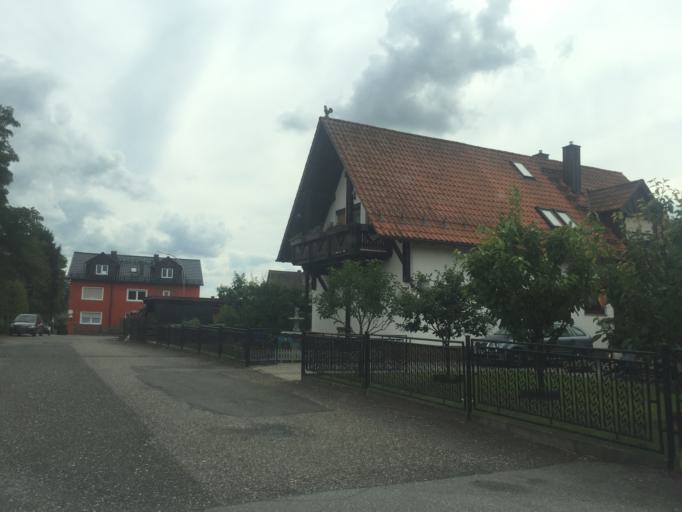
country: DE
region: Bavaria
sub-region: Upper Palatinate
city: Pressath
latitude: 49.7635
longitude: 11.9478
